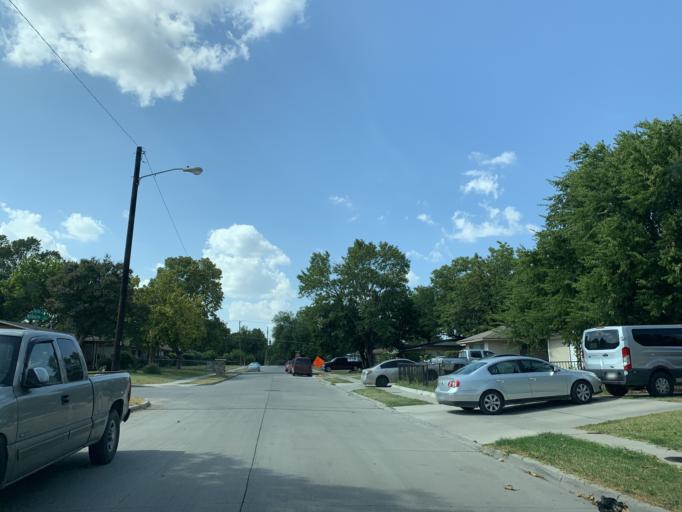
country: US
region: Texas
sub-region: Dallas County
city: Hutchins
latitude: 32.7025
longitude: -96.7729
